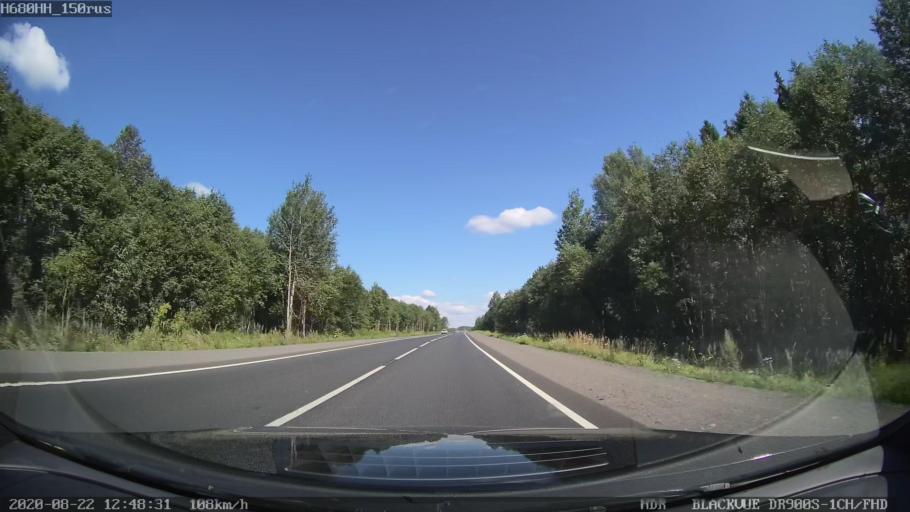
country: RU
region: Tverskaya
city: Rameshki
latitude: 57.4407
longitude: 36.1853
